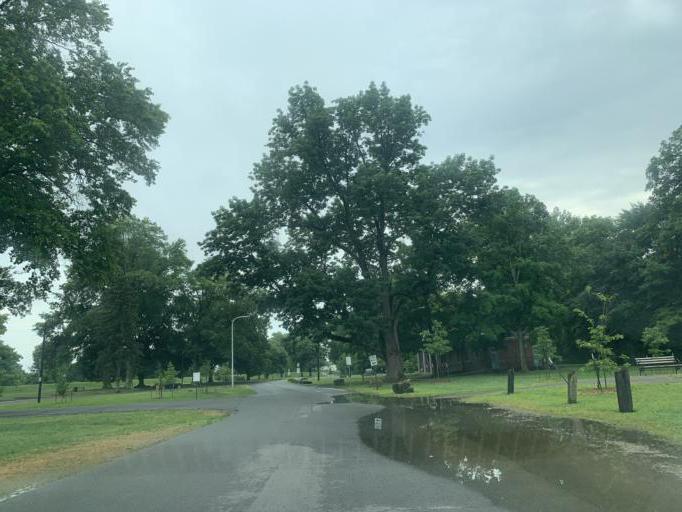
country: US
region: Kentucky
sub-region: Jefferson County
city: Shively
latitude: 38.2426
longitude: -85.8331
